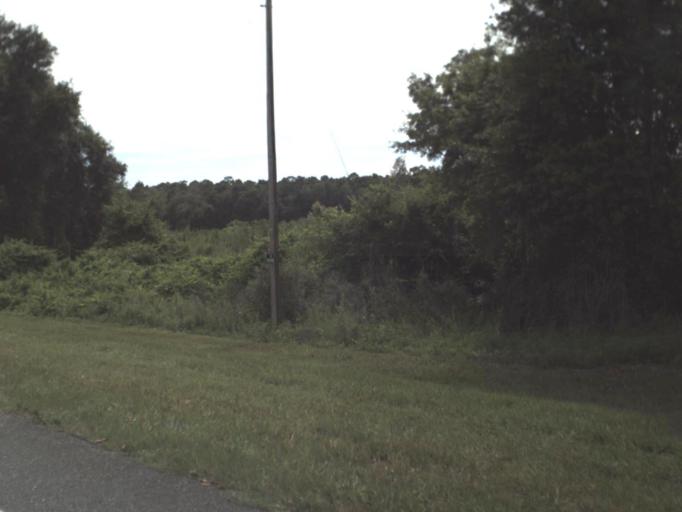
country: US
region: Florida
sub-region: Taylor County
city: Perry
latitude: 30.0838
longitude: -83.5002
